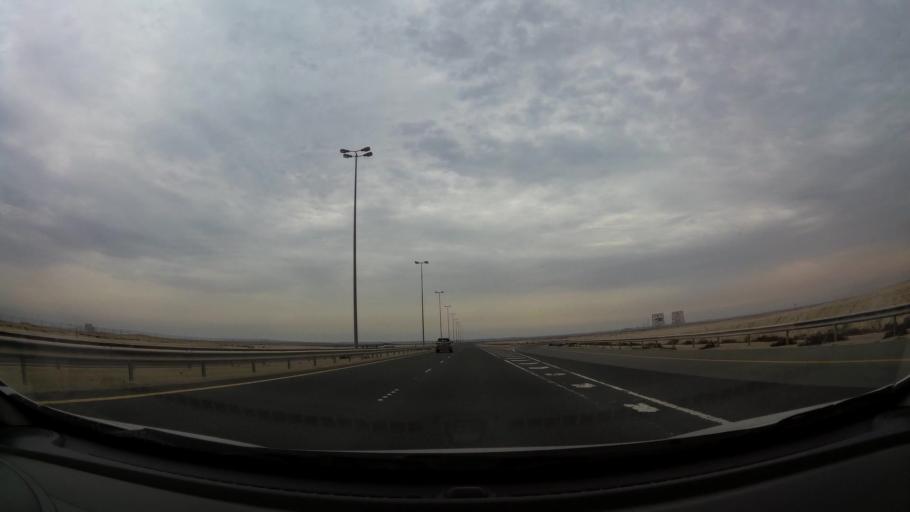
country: BH
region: Central Governorate
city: Dar Kulayb
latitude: 25.8730
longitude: 50.5797
